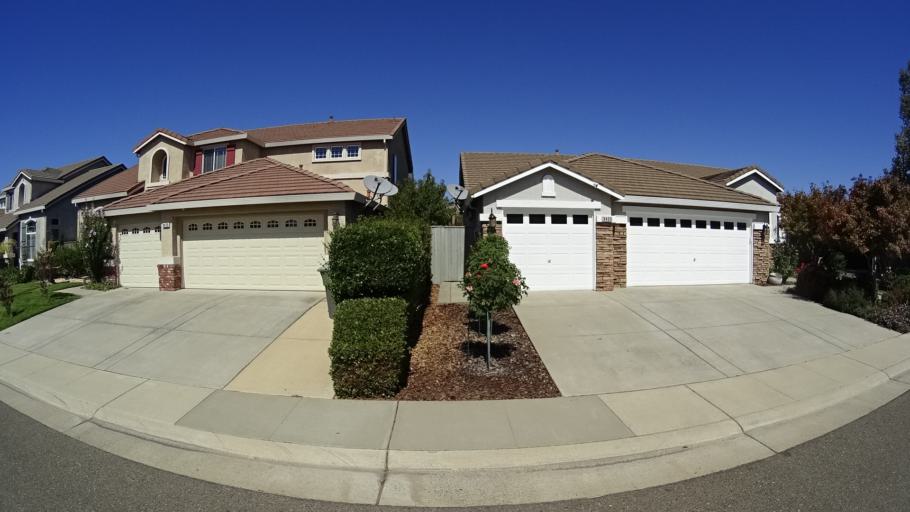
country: US
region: California
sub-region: Sacramento County
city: Elk Grove
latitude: 38.4023
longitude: -121.3464
